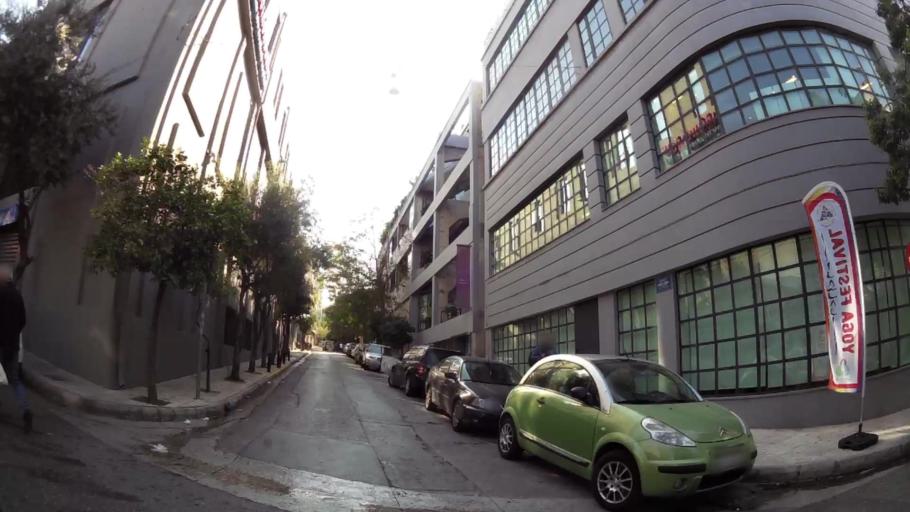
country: GR
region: Attica
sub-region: Nomarchia Athinas
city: Athens
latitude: 37.9745
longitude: 23.7104
